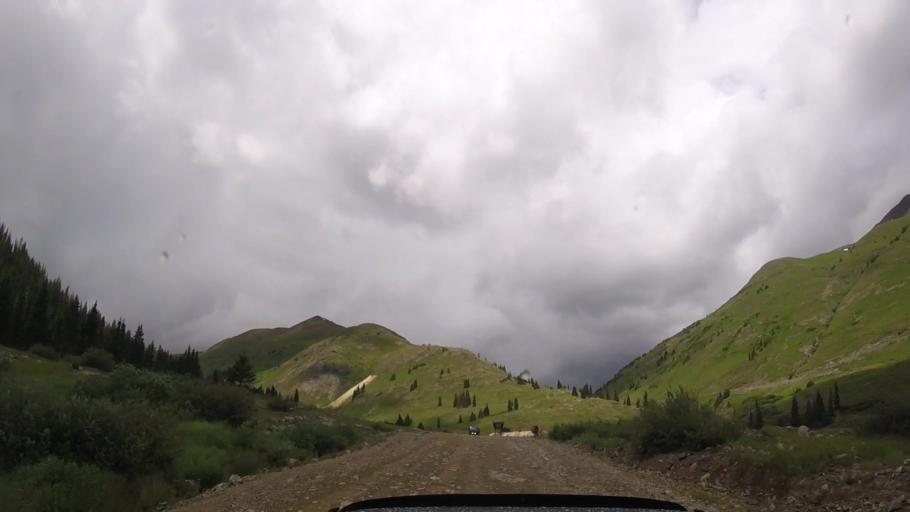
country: US
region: Colorado
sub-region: Ouray County
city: Ouray
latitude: 37.9303
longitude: -107.5699
